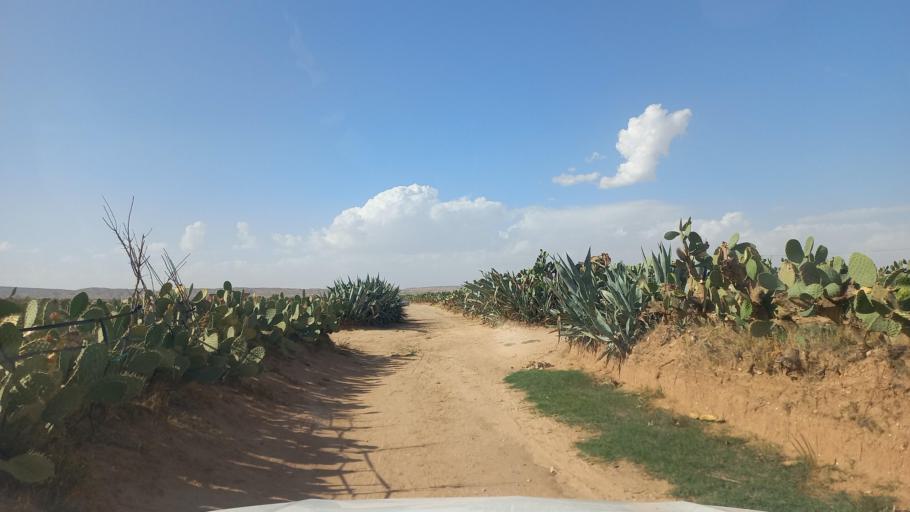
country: TN
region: Al Qasrayn
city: Sbiba
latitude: 35.3136
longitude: 9.0310
